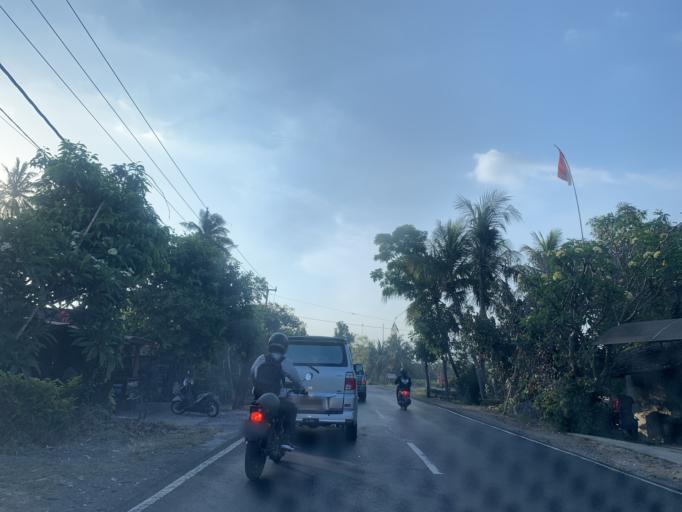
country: ID
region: Bali
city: Banjar Delodrurung
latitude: -8.4910
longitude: 114.9554
